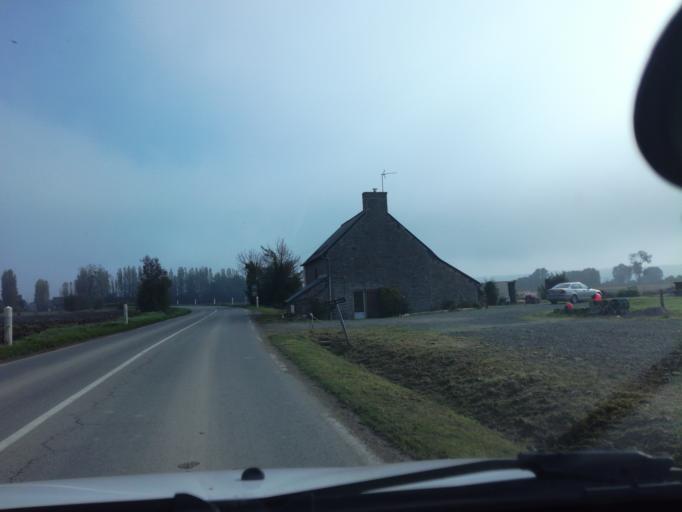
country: FR
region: Brittany
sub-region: Departement d'Ille-et-Vilaine
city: Cherrueix
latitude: 48.6002
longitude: -1.6901
